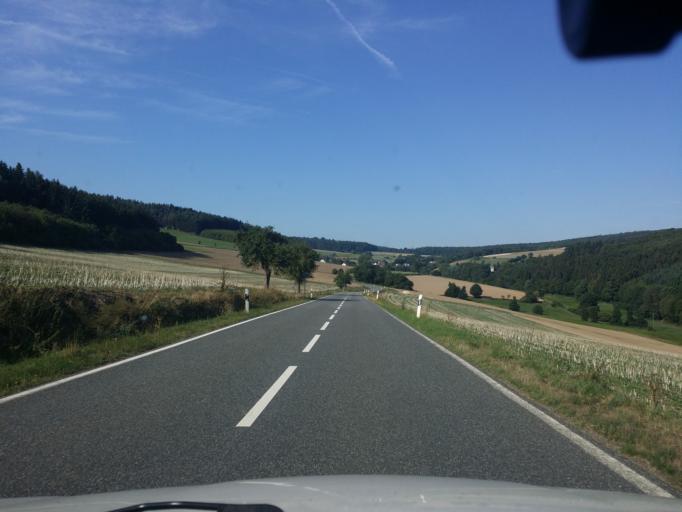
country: DE
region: Hesse
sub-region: Regierungsbezirk Darmstadt
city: Idstein
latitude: 50.2046
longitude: 8.2403
